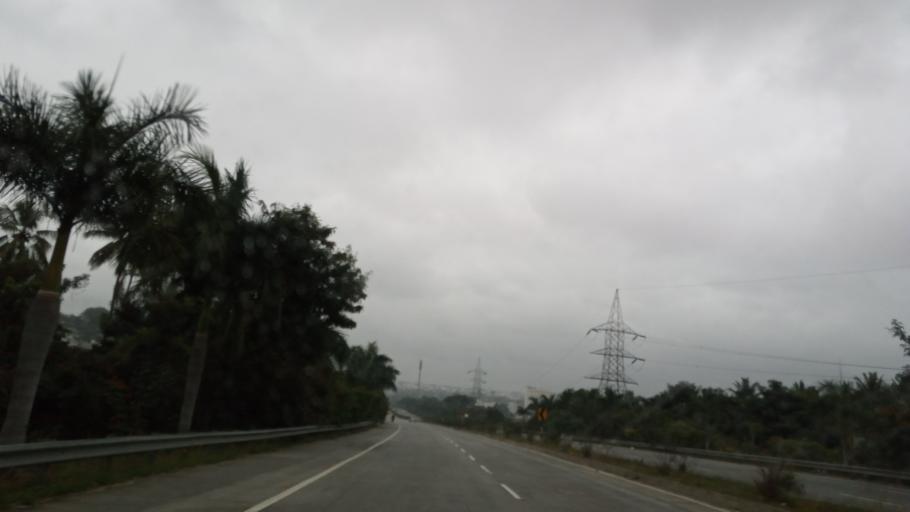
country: IN
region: Karnataka
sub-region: Bangalore Urban
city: Bangalore
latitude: 12.9225
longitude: 77.5321
